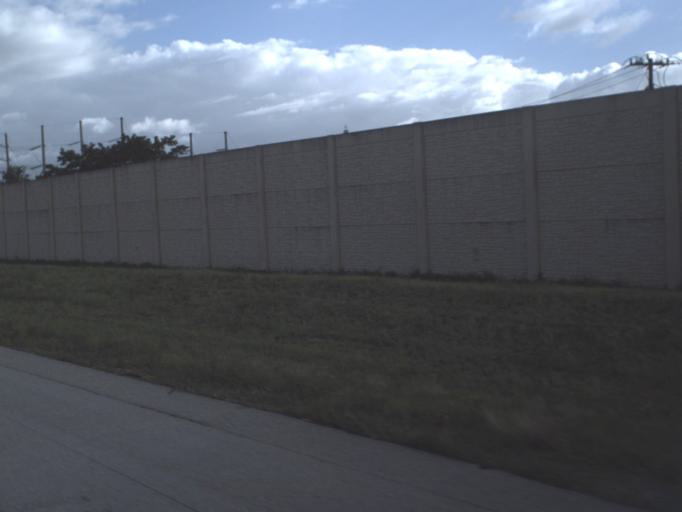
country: US
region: Florida
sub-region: Lee County
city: Bonita Springs
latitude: 26.3537
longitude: -81.7564
